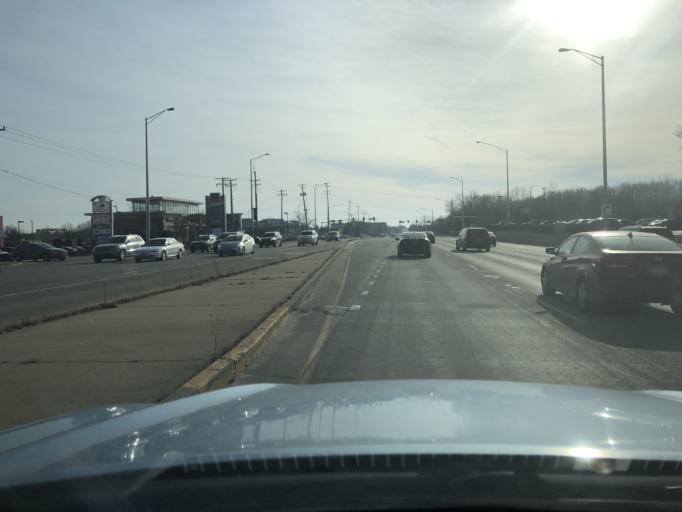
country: US
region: Illinois
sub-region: Cook County
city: South Barrington
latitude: 42.0625
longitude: -88.1448
